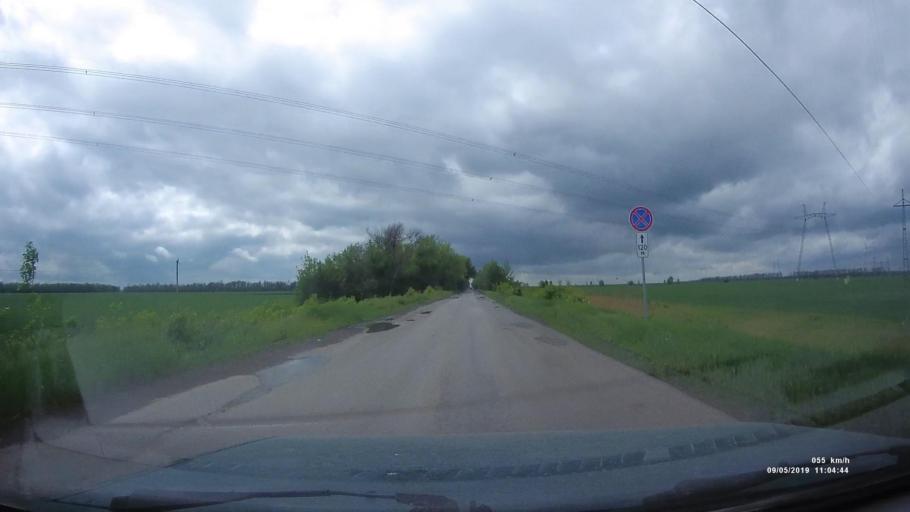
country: RU
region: Krasnodarskiy
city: Kanelovskaya
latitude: 46.8140
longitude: 39.2099
